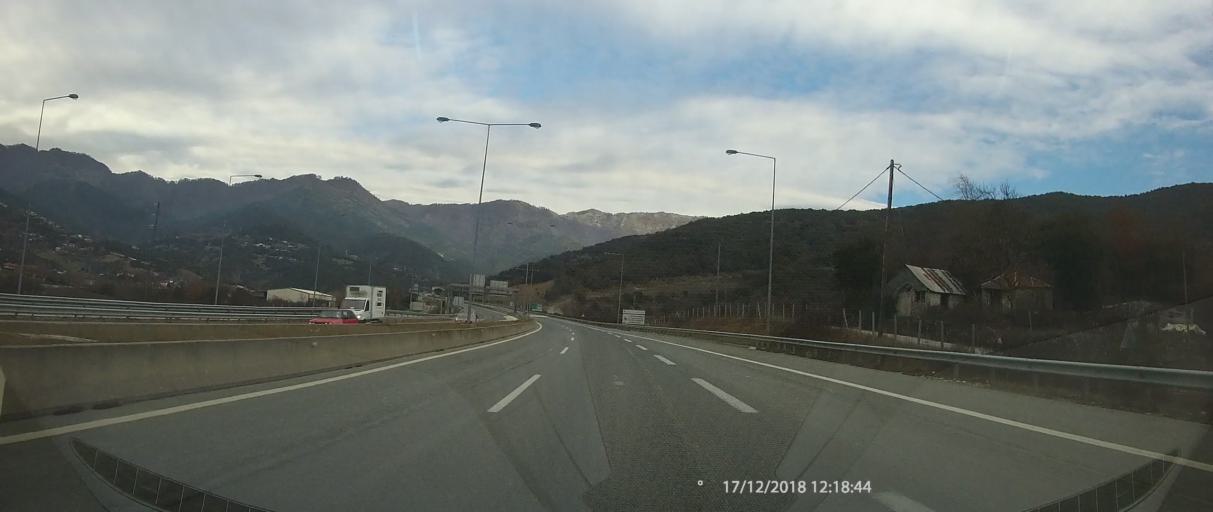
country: GR
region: Epirus
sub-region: Nomos Ioanninon
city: Metsovo
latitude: 39.7557
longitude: 21.0914
